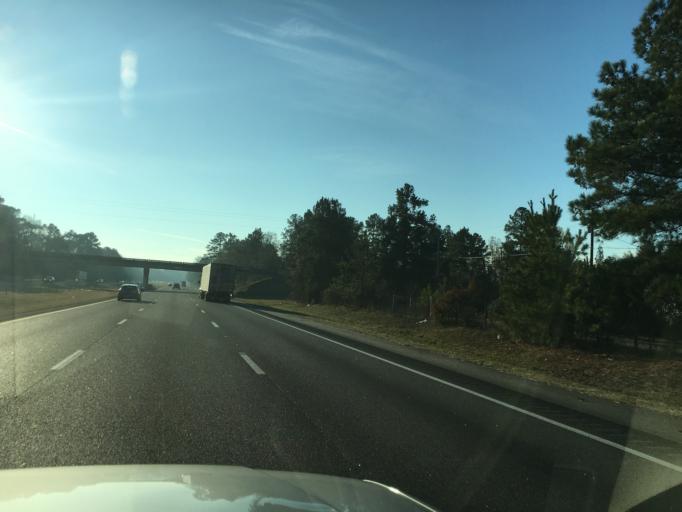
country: US
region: South Carolina
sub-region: Lexington County
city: Pineridge
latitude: 33.8947
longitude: -81.0442
